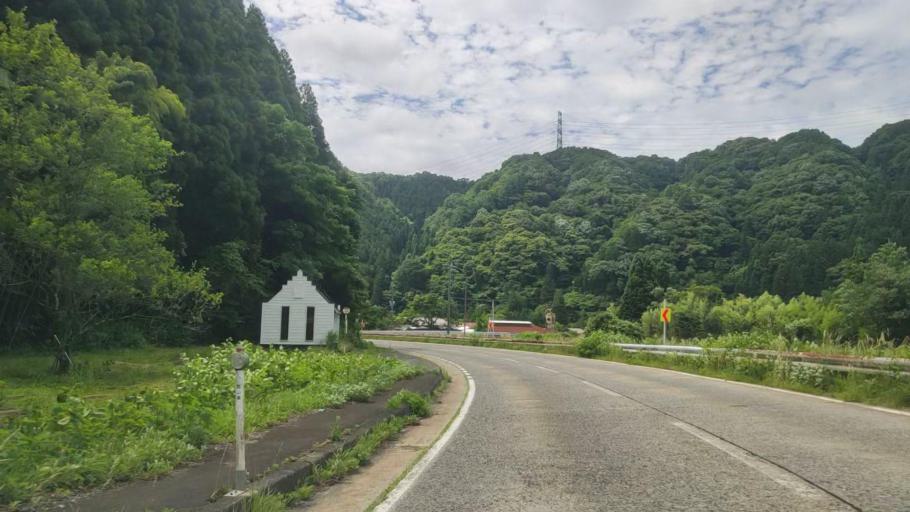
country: JP
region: Okayama
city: Niimi
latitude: 35.1642
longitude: 133.5792
